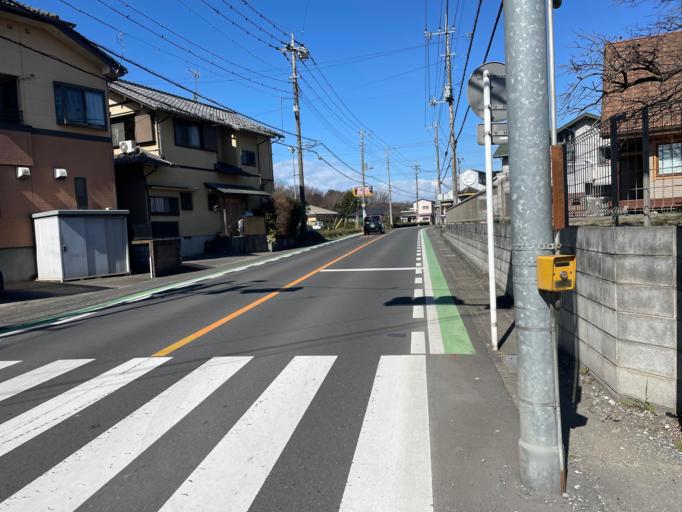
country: JP
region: Saitama
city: Sakado
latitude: 35.9544
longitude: 139.4335
